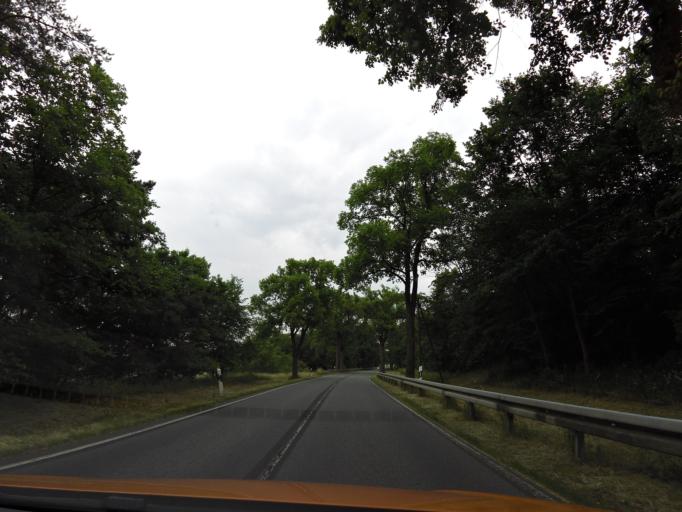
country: DE
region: Brandenburg
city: Rangsdorf
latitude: 52.2783
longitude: 13.3639
